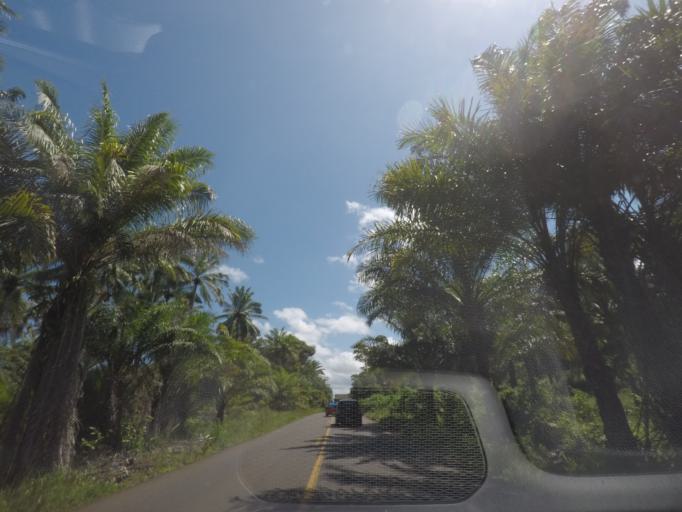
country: BR
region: Bahia
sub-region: Taperoa
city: Taperoa
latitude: -13.4732
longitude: -39.0890
